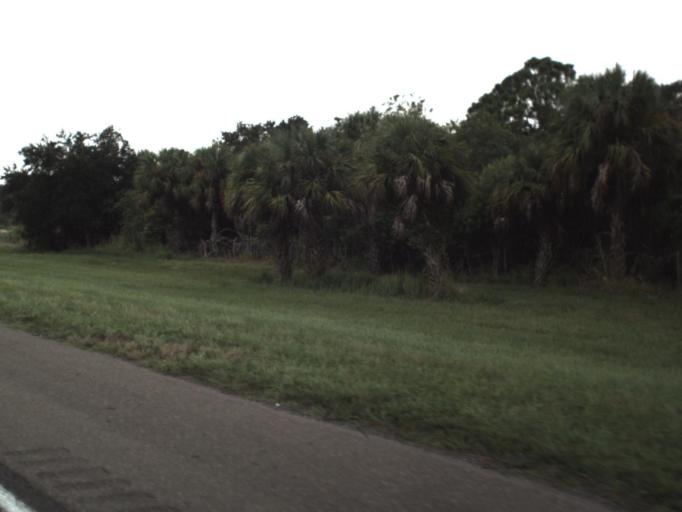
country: US
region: Florida
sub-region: Manatee County
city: Ellenton
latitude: 27.6075
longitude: -82.4974
